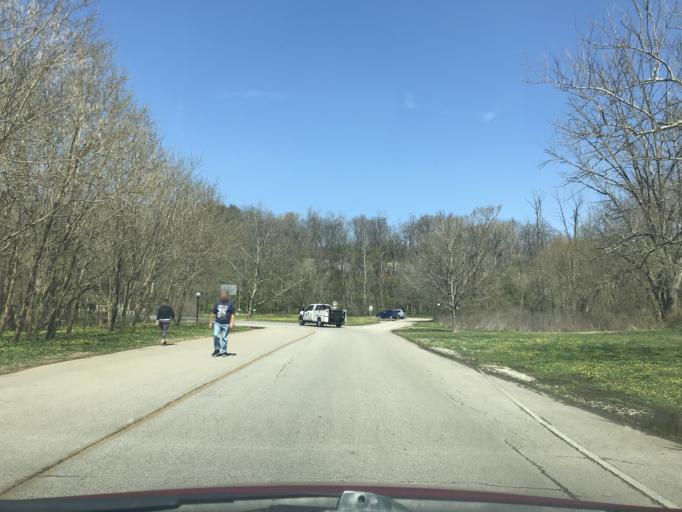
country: US
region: Kentucky
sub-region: Jefferson County
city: Saint Matthews
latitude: 38.2409
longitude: -85.6949
